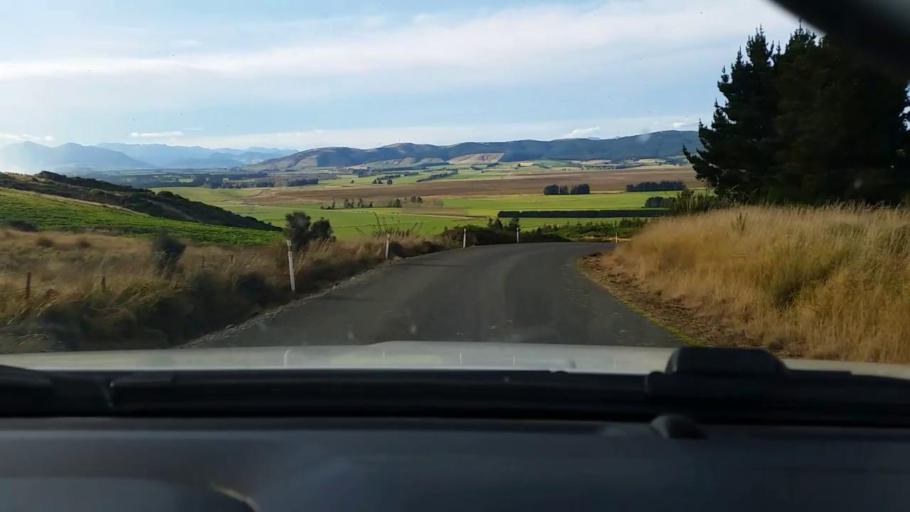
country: NZ
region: Southland
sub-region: Southland District
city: Winton
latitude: -45.8191
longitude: 168.1743
